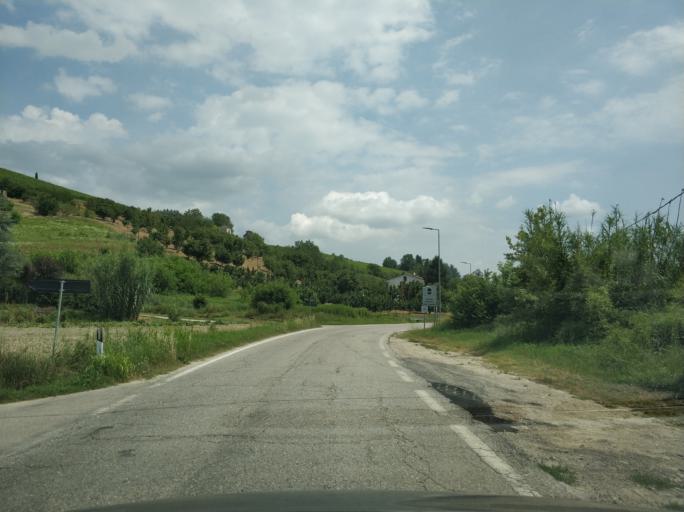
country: IT
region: Piedmont
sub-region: Provincia di Cuneo
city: Canale
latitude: 44.7930
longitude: 7.9770
